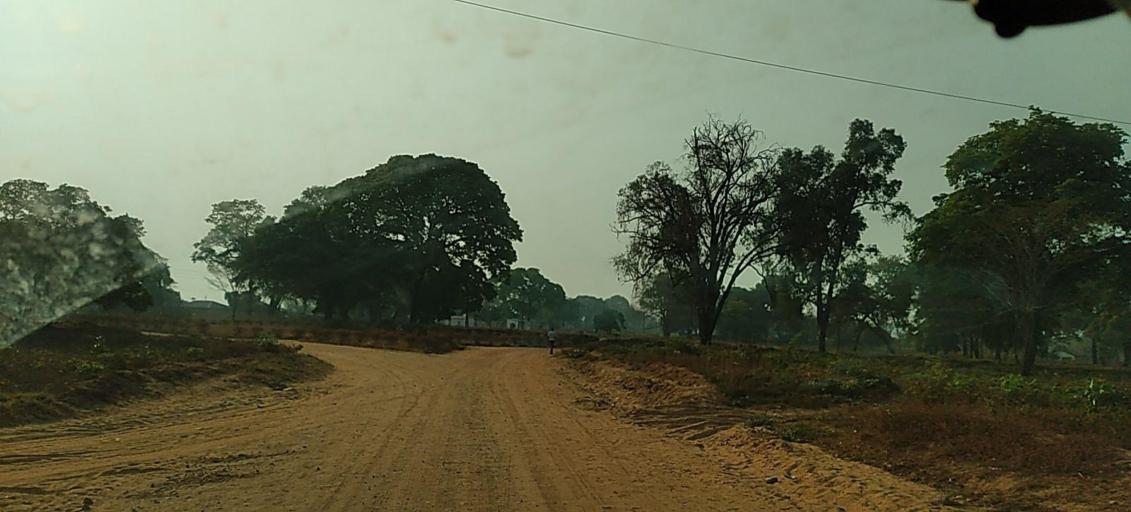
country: ZM
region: North-Western
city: Kabompo
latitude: -13.5981
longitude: 24.2071
